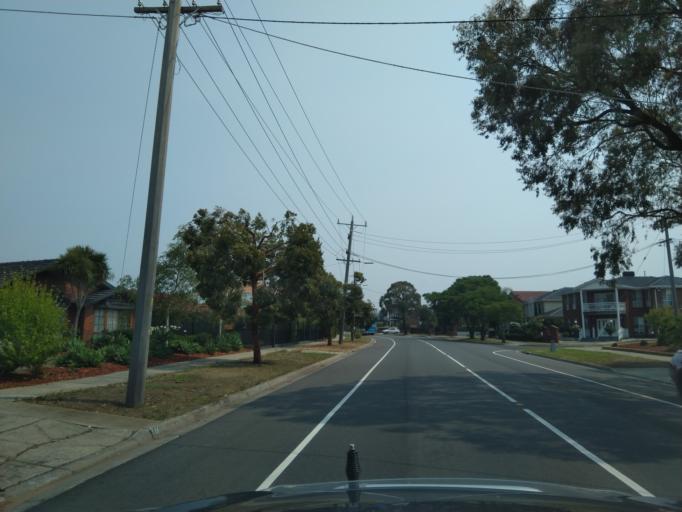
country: AU
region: Victoria
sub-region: Hume
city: Meadow Heights
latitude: -37.6449
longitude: 144.8979
